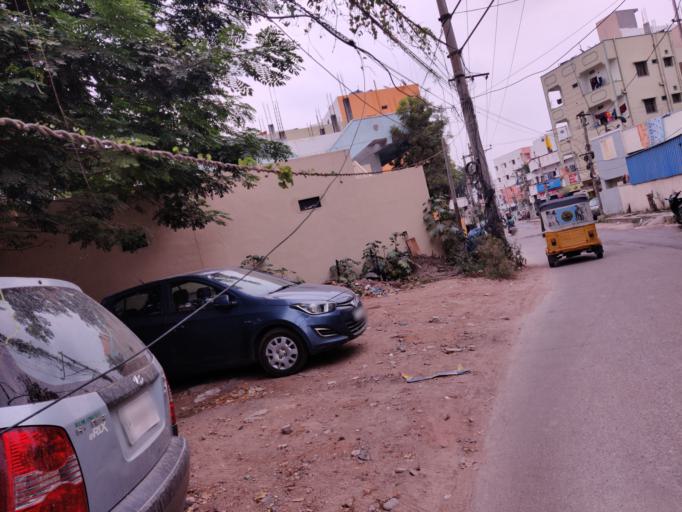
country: IN
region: Telangana
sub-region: Hyderabad
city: Hyderabad
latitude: 17.4056
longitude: 78.3969
